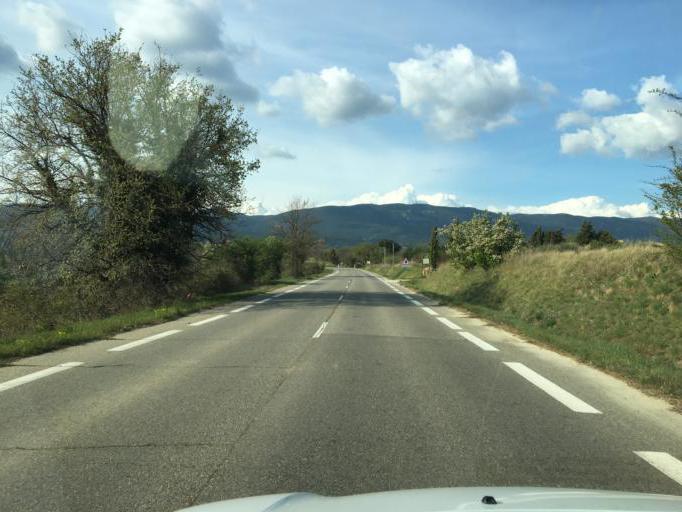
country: FR
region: Provence-Alpes-Cote d'Azur
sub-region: Departement du Vaucluse
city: Ansouis
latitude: 43.7538
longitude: 5.4610
